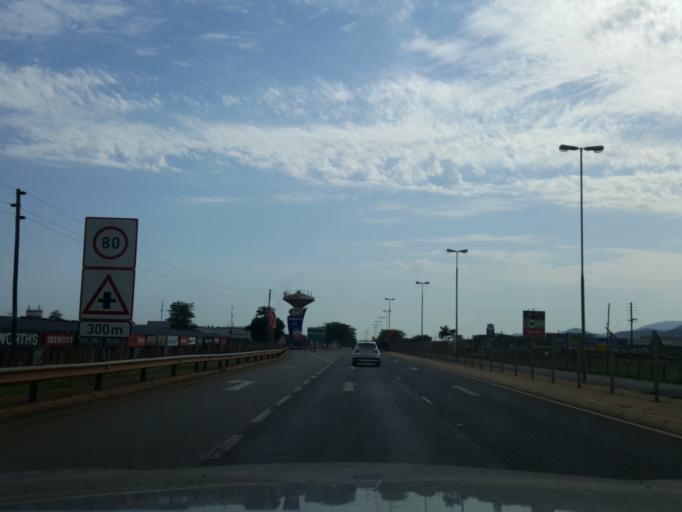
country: SZ
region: Hhohho
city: Ntfonjeni
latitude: -25.5010
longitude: 31.5057
